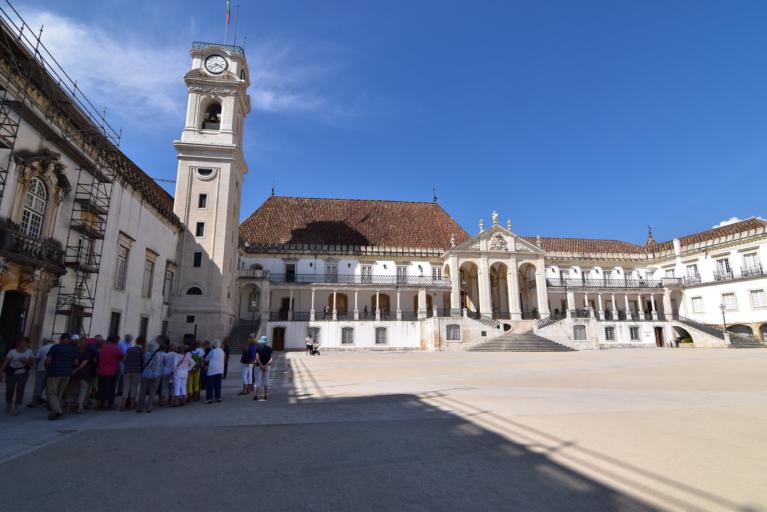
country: PT
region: Coimbra
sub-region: Coimbra
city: Coimbra
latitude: 40.2074
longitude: -8.4263
